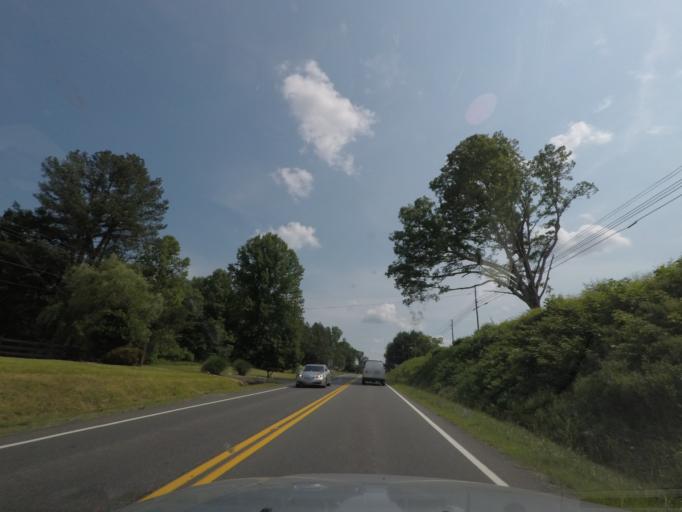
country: US
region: Virginia
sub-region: Fluvanna County
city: Palmyra
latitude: 37.8504
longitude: -78.2719
